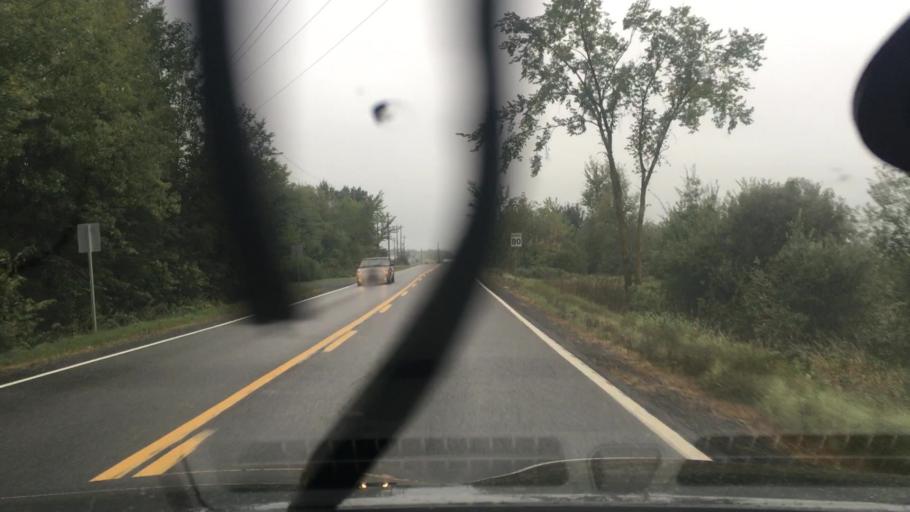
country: CA
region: Nova Scotia
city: Windsor
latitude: 44.9766
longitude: -64.1338
